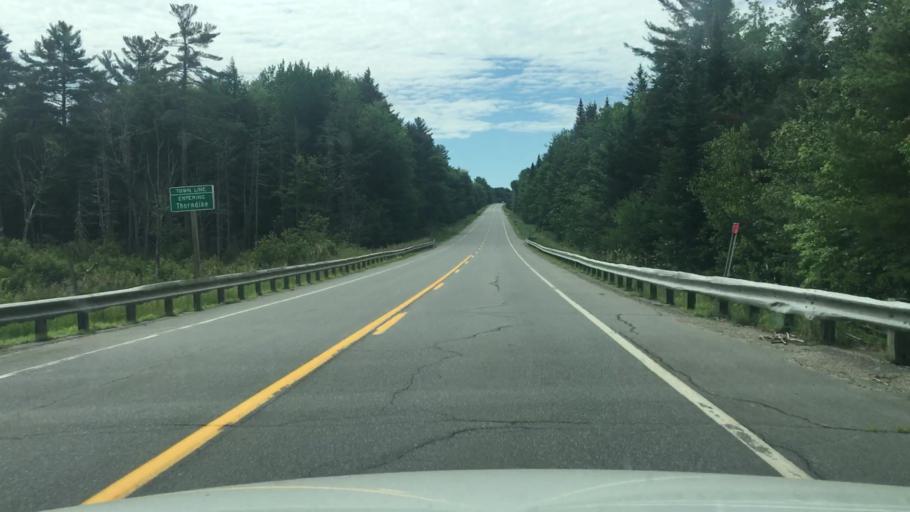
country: US
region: Maine
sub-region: Waldo County
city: Troy
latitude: 44.5960
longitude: -69.2848
